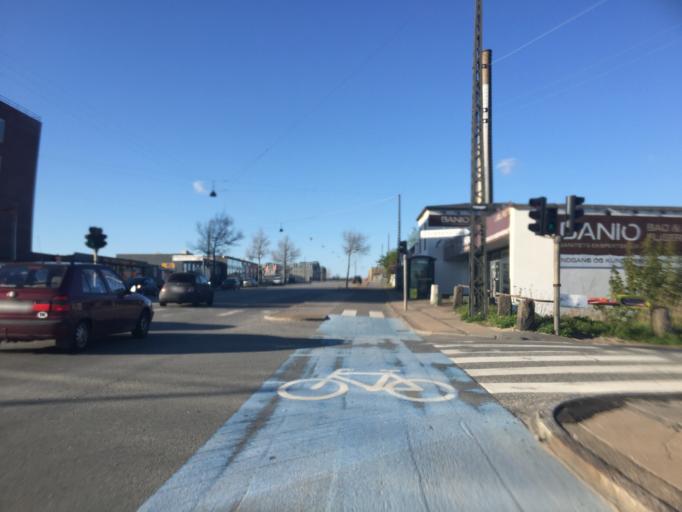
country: DK
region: Capital Region
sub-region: Frederiksberg Kommune
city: Frederiksberg
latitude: 55.6533
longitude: 12.5102
